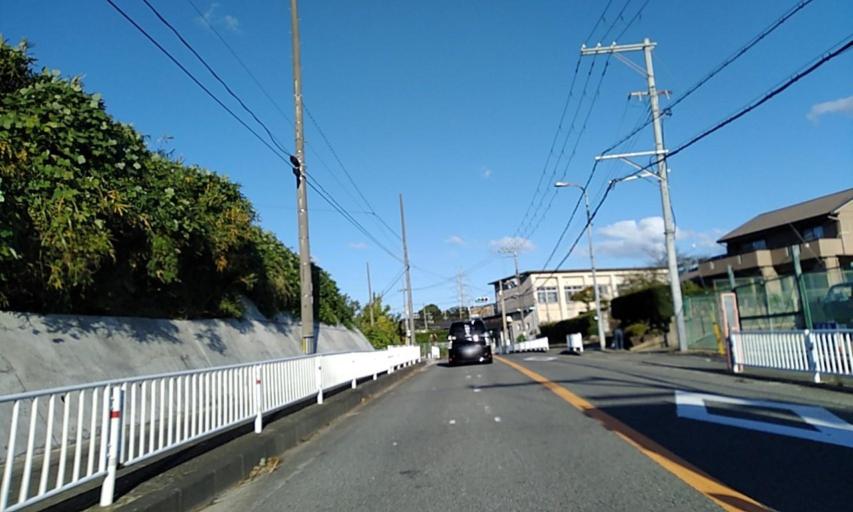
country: JP
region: Wakayama
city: Wakayama-shi
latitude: 34.3155
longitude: 135.1302
